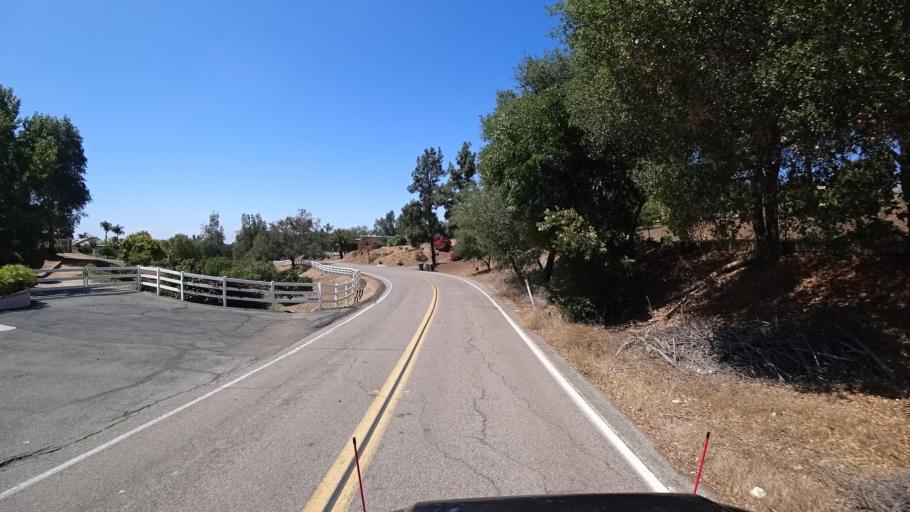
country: US
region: California
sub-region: San Diego County
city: Fallbrook
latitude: 33.3810
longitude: -117.2154
